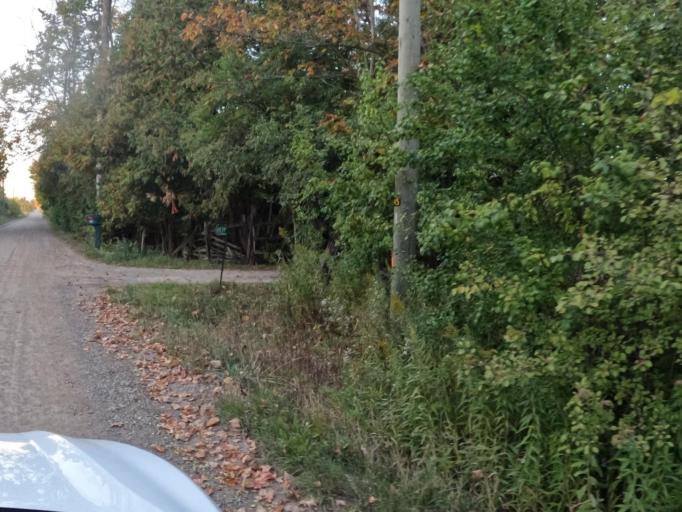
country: CA
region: Ontario
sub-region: Wellington County
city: Guelph
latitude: 43.5653
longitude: -80.1663
